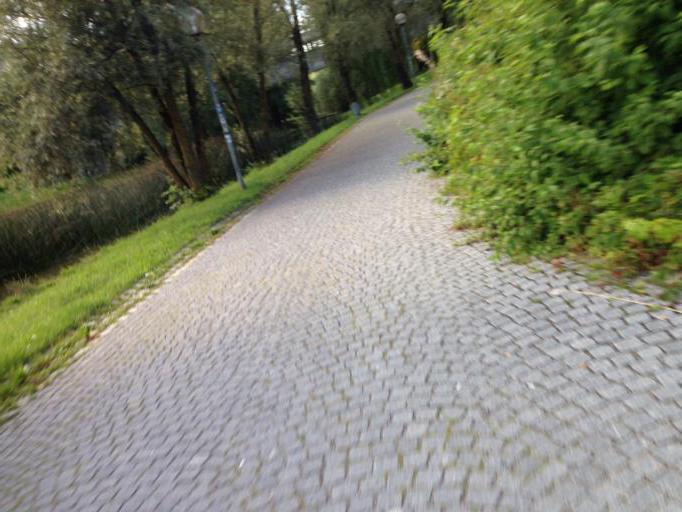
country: DE
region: Bavaria
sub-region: Swabia
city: Augsburg
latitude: 48.3342
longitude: 10.8960
